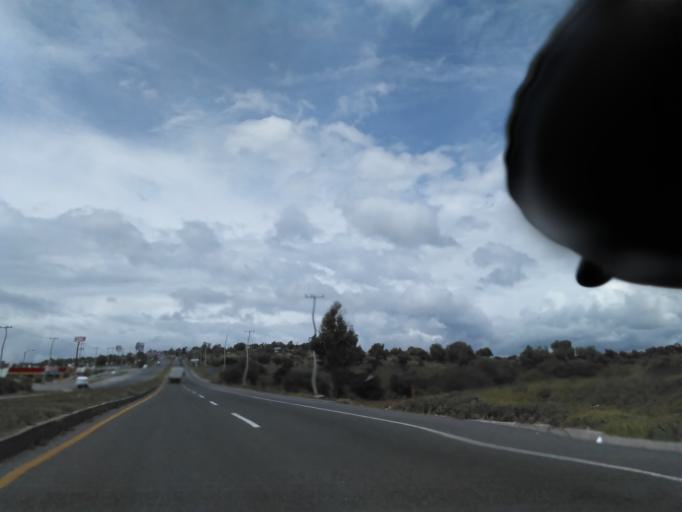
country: MX
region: Hidalgo
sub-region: Atotonilco de Tula
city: Paseos de la Pradera
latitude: 19.9228
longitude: -99.2377
